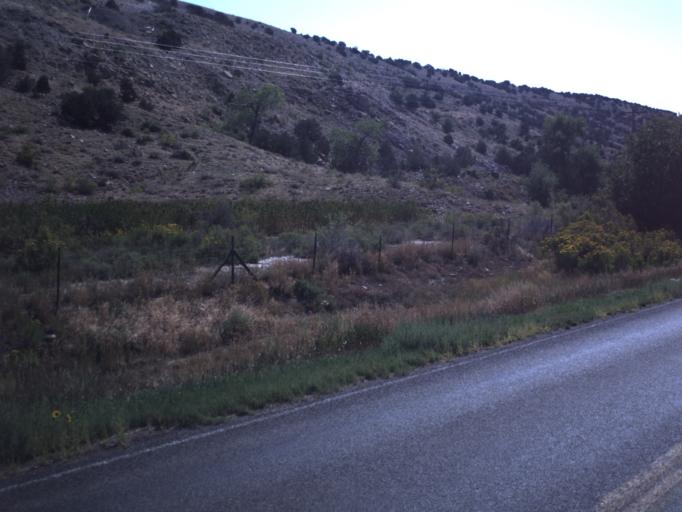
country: US
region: Utah
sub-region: Duchesne County
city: Duchesne
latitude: 40.2677
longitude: -110.4195
